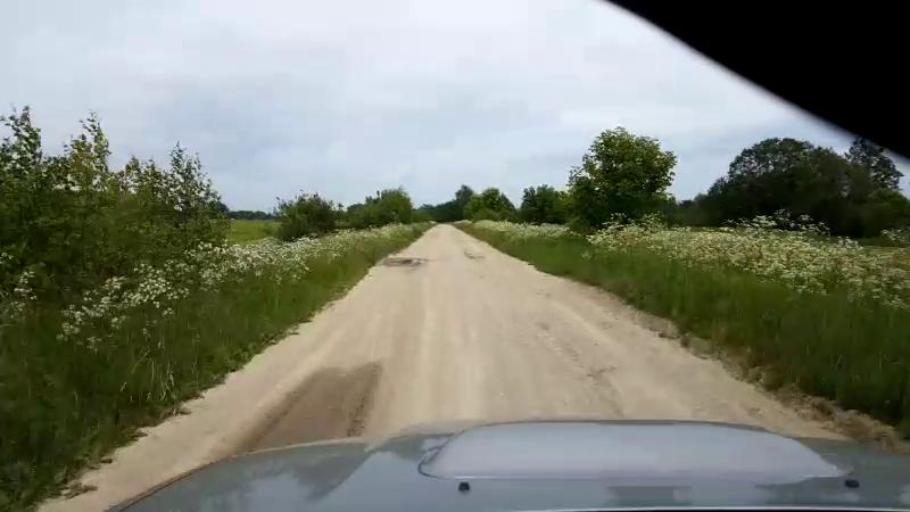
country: EE
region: Paernumaa
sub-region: Sindi linn
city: Sindi
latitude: 58.5153
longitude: 24.6077
